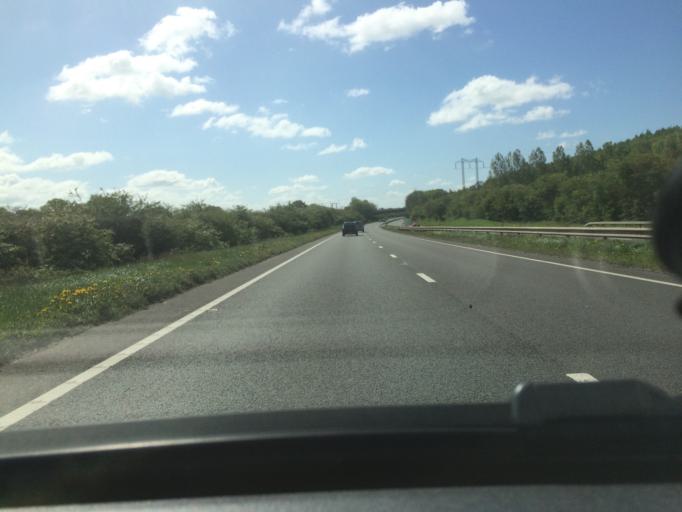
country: GB
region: Wales
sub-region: Wrexham
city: Rhosllanerchrugog
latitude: 53.0201
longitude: -3.0256
